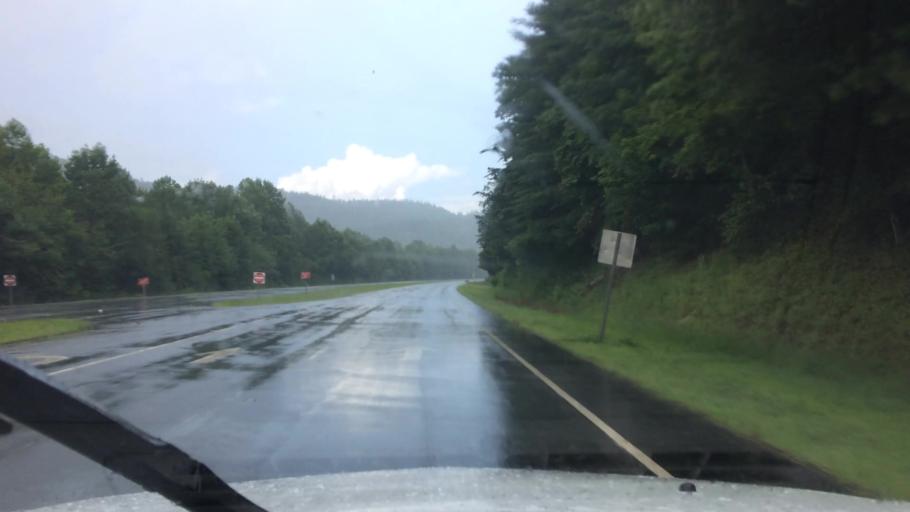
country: US
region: North Carolina
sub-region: Wilkes County
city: Millers Creek
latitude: 36.1944
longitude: -81.4216
